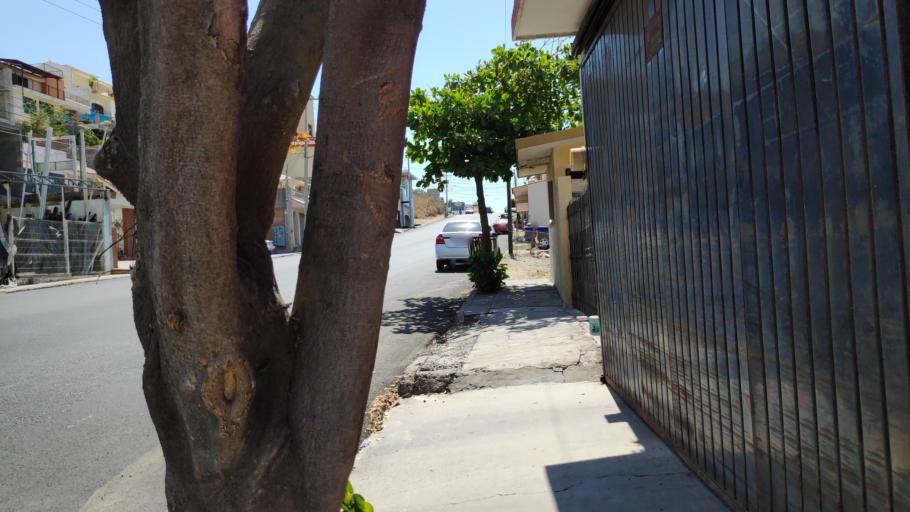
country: MX
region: Sinaloa
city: Culiacan
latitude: 24.7847
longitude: -107.4017
